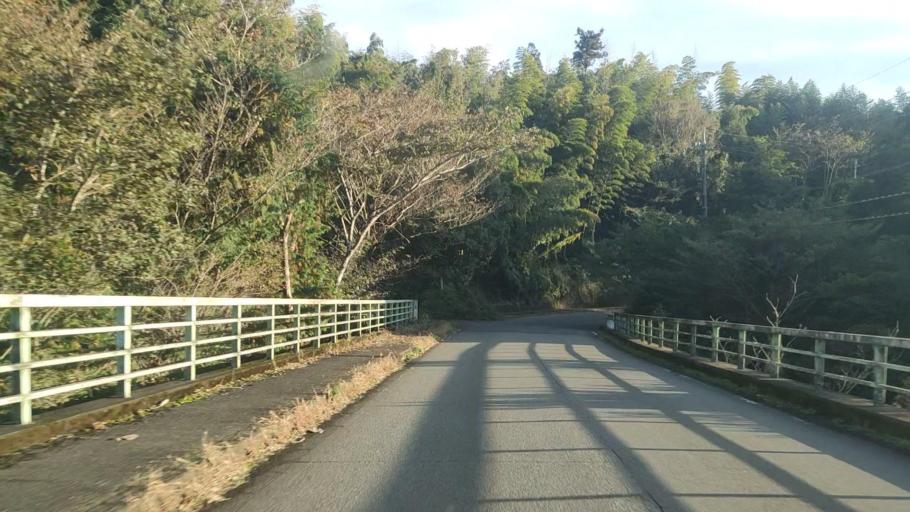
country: JP
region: Shizuoka
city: Mishima
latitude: 35.1396
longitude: 138.9612
